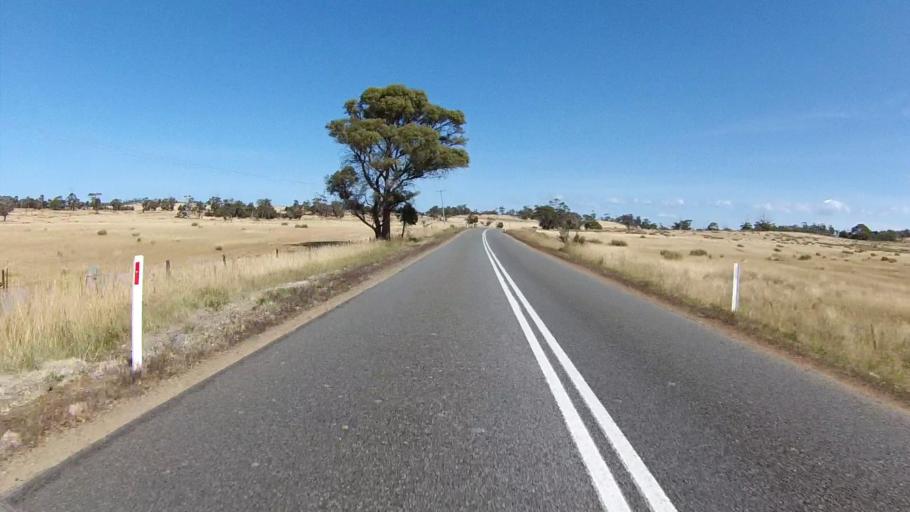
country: AU
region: Tasmania
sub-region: Sorell
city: Sorell
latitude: -42.2933
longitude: 147.9895
